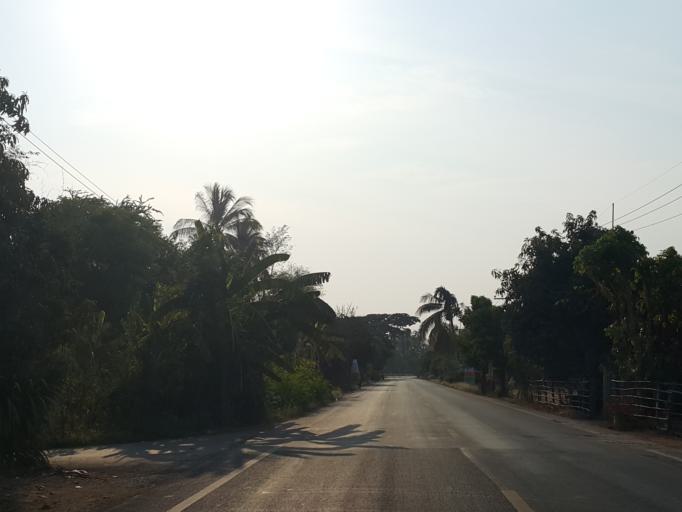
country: TH
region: Uttaradit
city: Phichai
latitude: 17.1680
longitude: 100.0929
